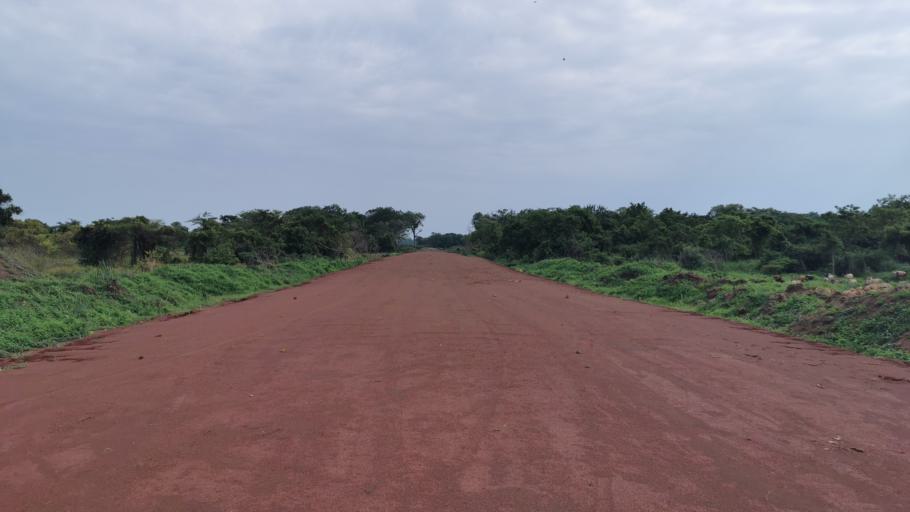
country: ET
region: Gambela
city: Gambela
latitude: 7.8725
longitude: 34.4959
